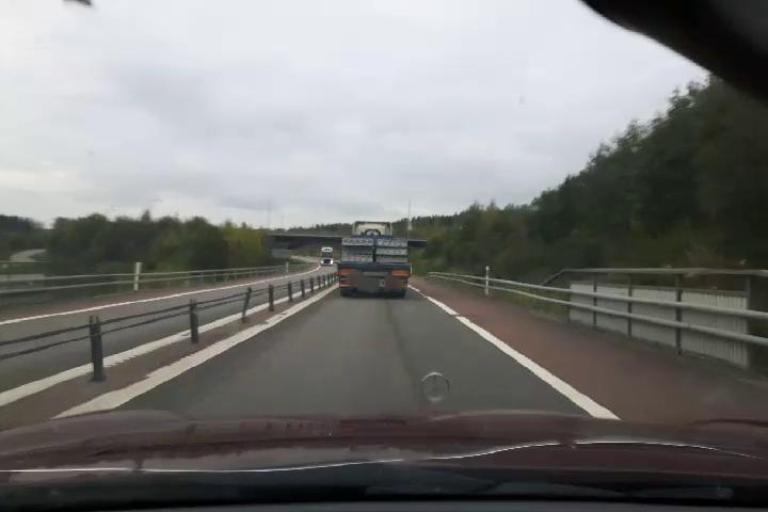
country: SE
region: Vaesternorrland
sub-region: Haernoesands Kommun
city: Haernoesand
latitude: 62.7832
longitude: 17.9186
